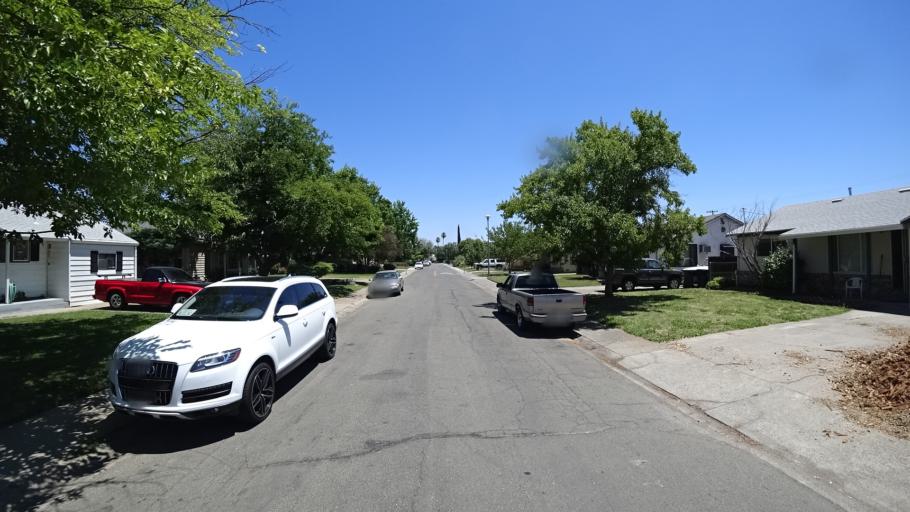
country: US
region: California
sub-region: Sacramento County
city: Parkway
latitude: 38.5305
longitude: -121.4771
